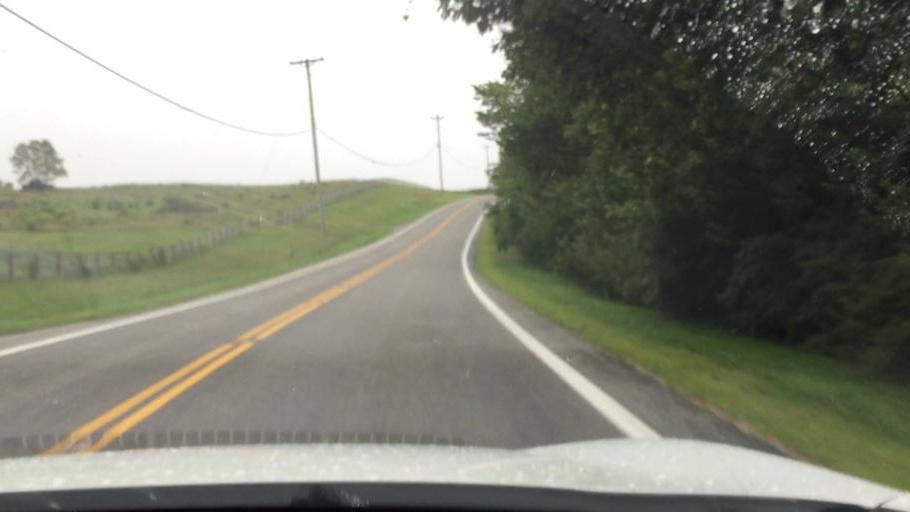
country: US
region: Ohio
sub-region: Champaign County
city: Mechanicsburg
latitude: 40.0193
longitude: -83.6358
